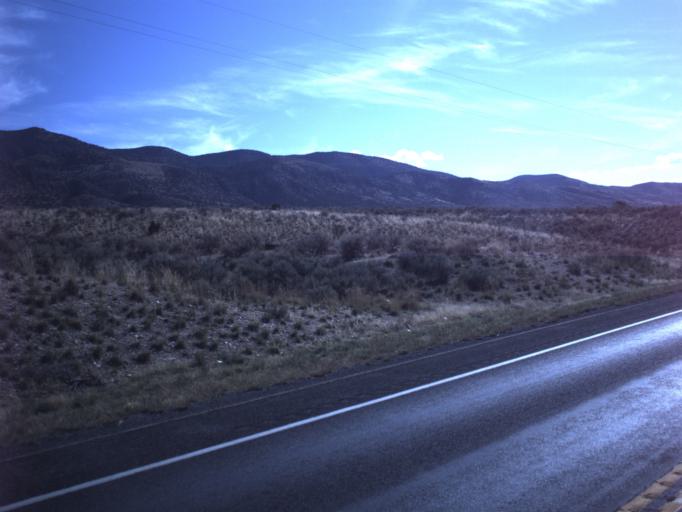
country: US
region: Utah
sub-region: Sanpete County
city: Gunnison
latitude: 39.2788
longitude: -111.8781
